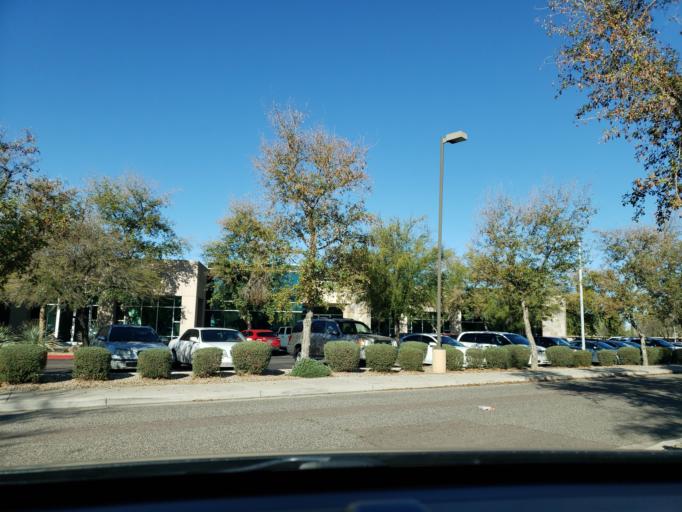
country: US
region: Arizona
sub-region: Maricopa County
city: Glendale
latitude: 33.6370
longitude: -112.1179
